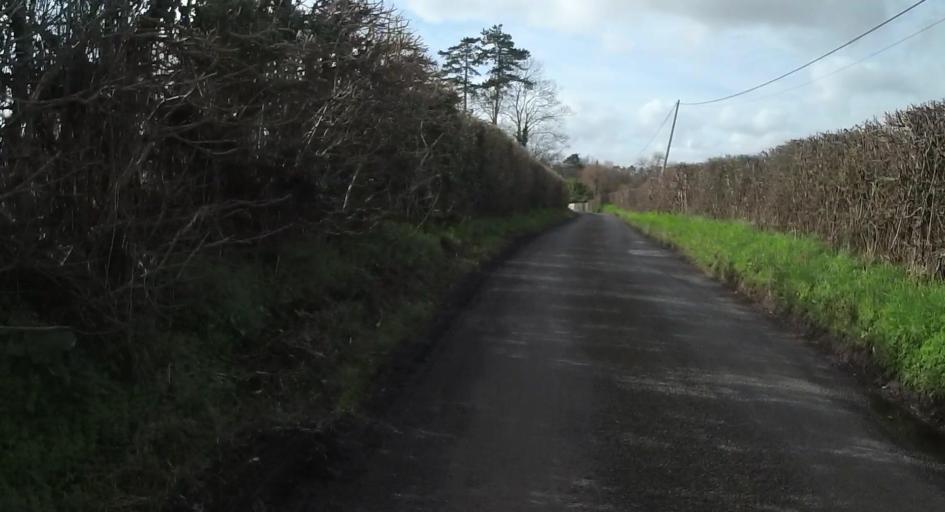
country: GB
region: England
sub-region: Hampshire
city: Kingsclere
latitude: 51.3521
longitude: -1.2476
